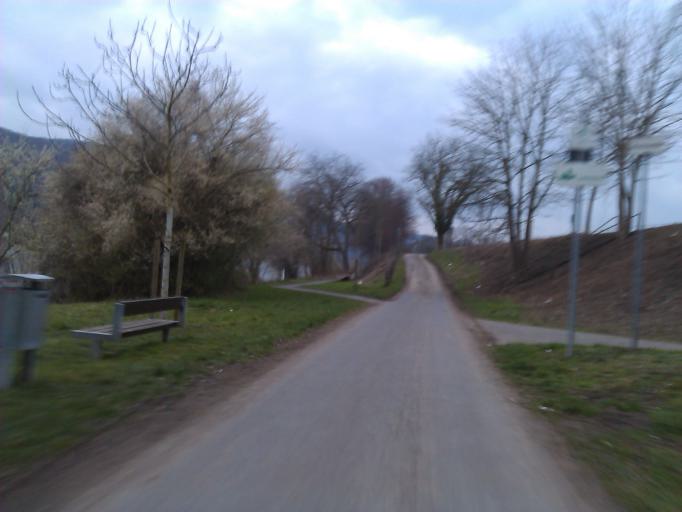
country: DE
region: Rheinland-Pfalz
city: Lahnstein
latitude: 50.2941
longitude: 7.6086
